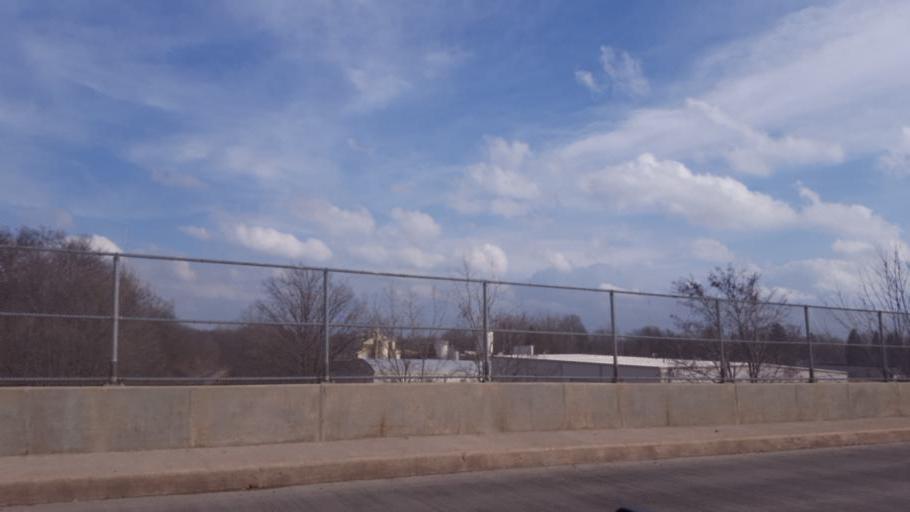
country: US
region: Ohio
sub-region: Richland County
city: Mansfield
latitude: 40.7709
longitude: -82.5517
